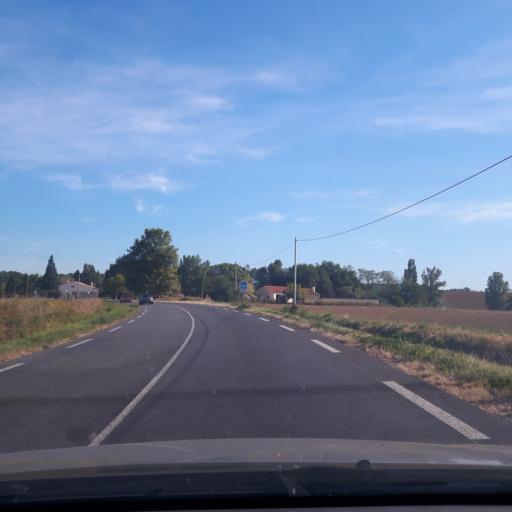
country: FR
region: Midi-Pyrenees
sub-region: Departement de la Haute-Garonne
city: Cepet
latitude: 43.7601
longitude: 1.4415
